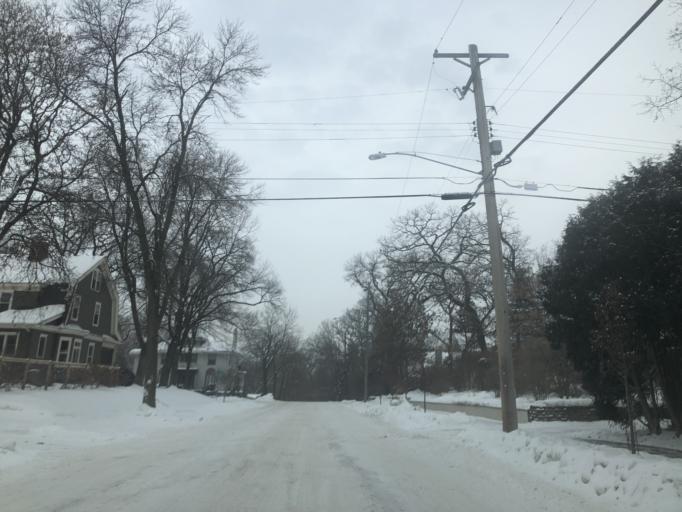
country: US
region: Minnesota
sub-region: Hennepin County
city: Richfield
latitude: 44.9160
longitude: -93.2951
